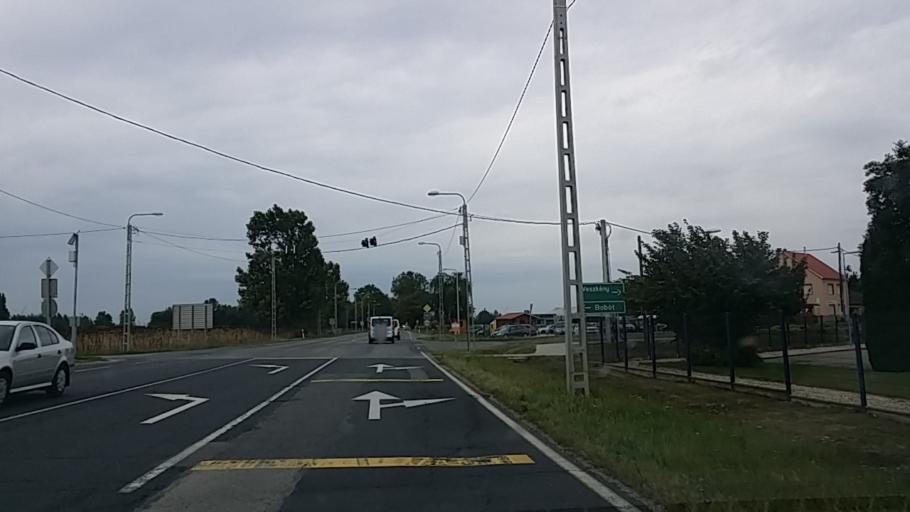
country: HU
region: Gyor-Moson-Sopron
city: Kapuvar
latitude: 47.5875
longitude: 17.0997
